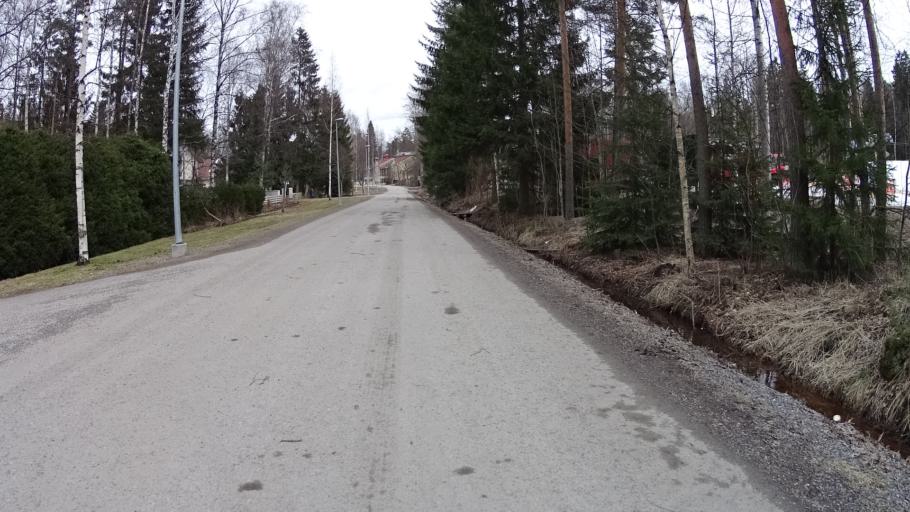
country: FI
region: Uusimaa
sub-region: Helsinki
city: Kauniainen
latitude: 60.2217
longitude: 24.7025
